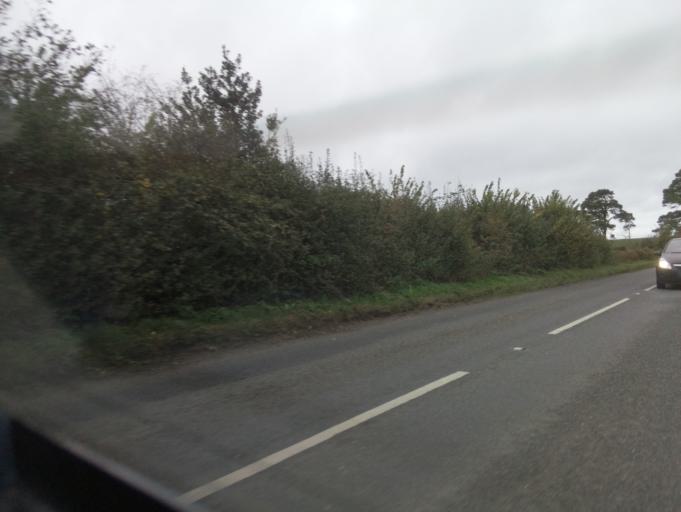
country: GB
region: England
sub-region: Dorset
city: Sherborne
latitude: 50.9679
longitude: -2.5519
